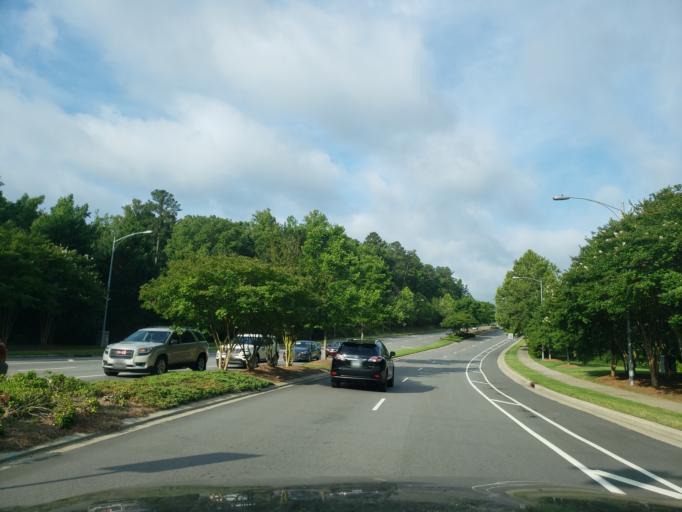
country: US
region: North Carolina
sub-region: Durham County
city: Durham
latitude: 35.9479
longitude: -78.9242
